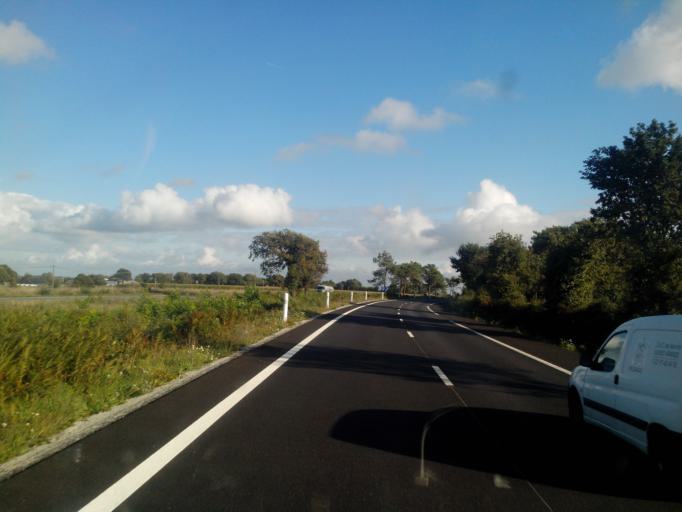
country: FR
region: Brittany
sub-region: Departement du Morbihan
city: Ambon
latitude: 47.5739
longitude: -2.5215
